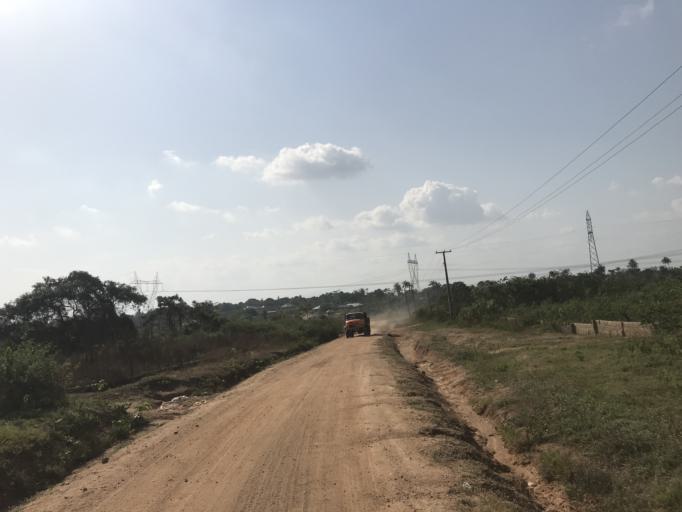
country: NG
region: Osun
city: Osogbo
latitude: 7.8432
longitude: 4.5783
